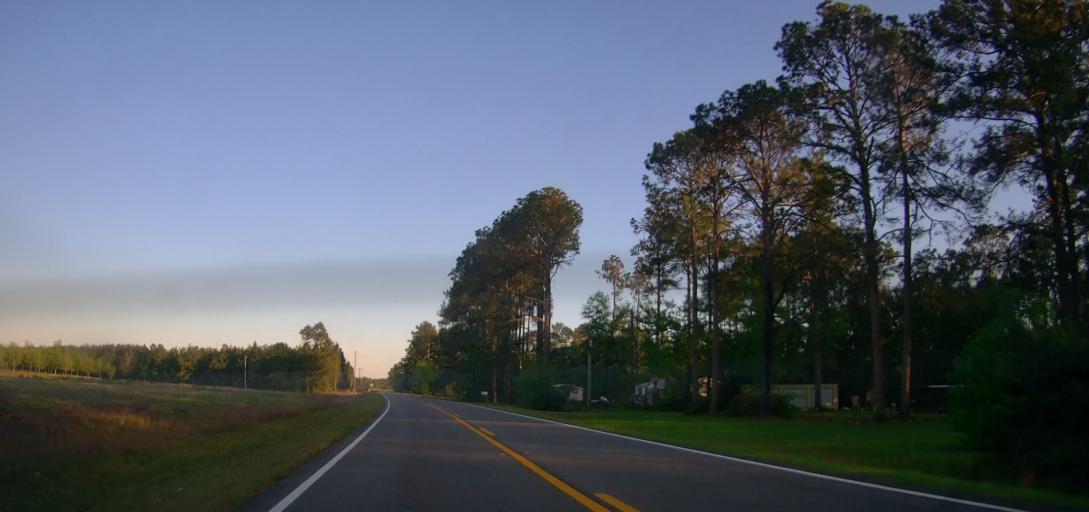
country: US
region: Georgia
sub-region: Irwin County
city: Ocilla
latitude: 31.6208
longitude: -83.2701
